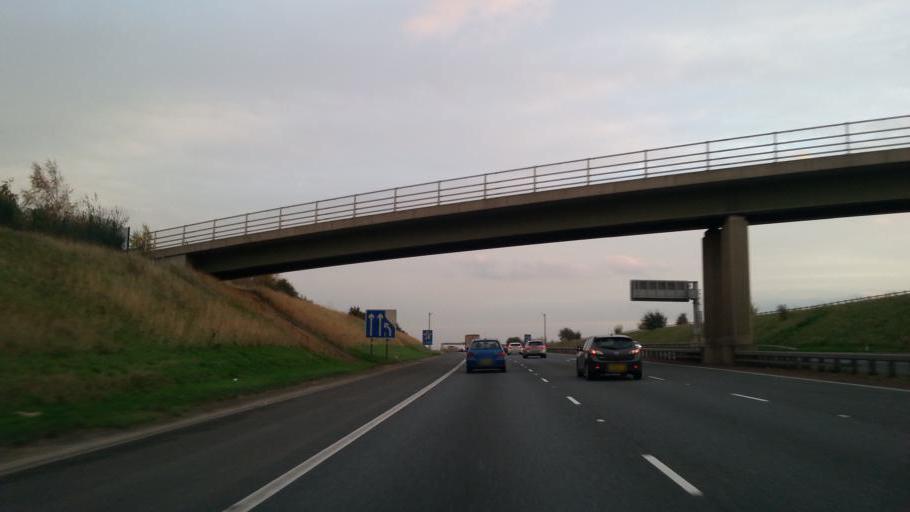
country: GB
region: England
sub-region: City and Borough of Wakefield
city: Darrington
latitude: 53.6919
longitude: -1.2734
